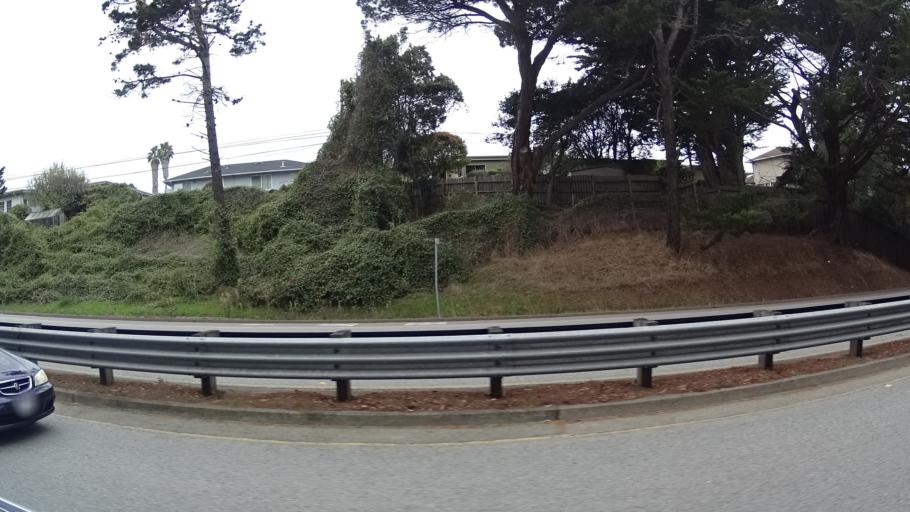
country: US
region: California
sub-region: San Mateo County
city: Colma
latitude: 37.6489
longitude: -122.4432
